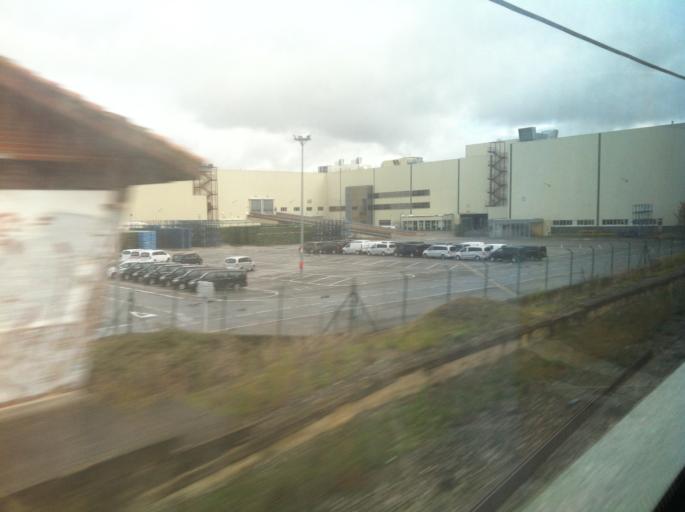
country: ES
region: Basque Country
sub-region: Provincia de Alava
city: Gasteiz / Vitoria
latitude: 42.8543
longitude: -2.7192
